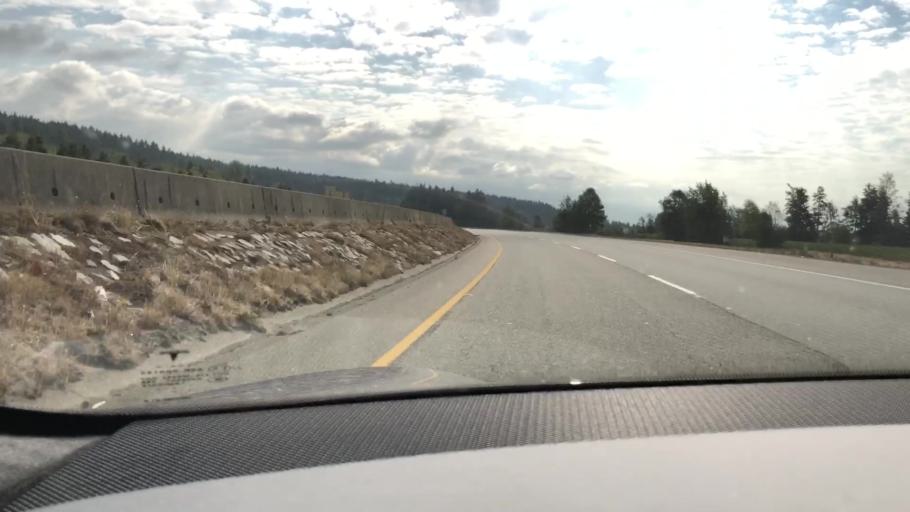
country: CA
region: British Columbia
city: Delta
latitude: 49.1156
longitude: -122.9221
